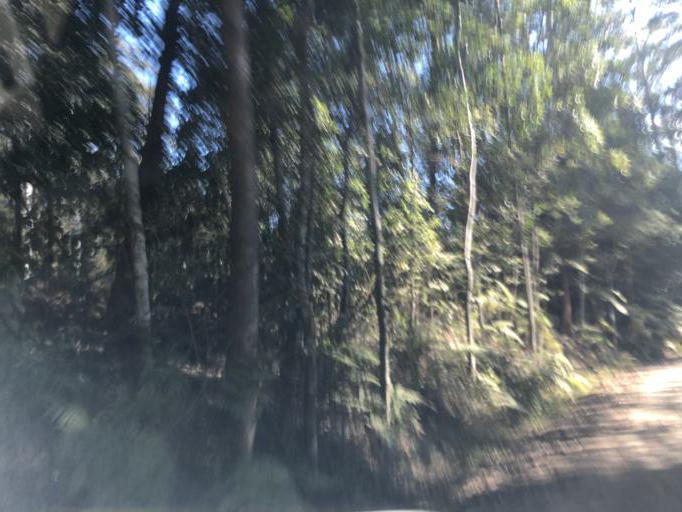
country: AU
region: New South Wales
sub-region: Bellingen
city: Bellingen
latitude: -30.4371
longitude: 152.8278
